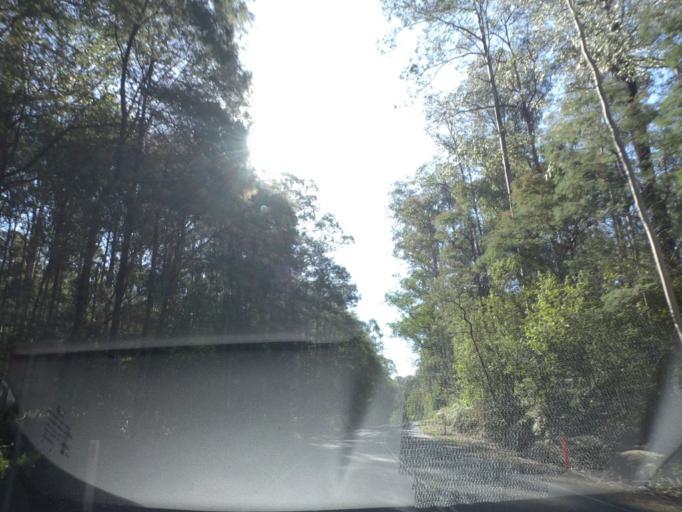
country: AU
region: Victoria
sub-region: Yarra Ranges
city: Millgrove
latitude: -37.8867
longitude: 145.8909
